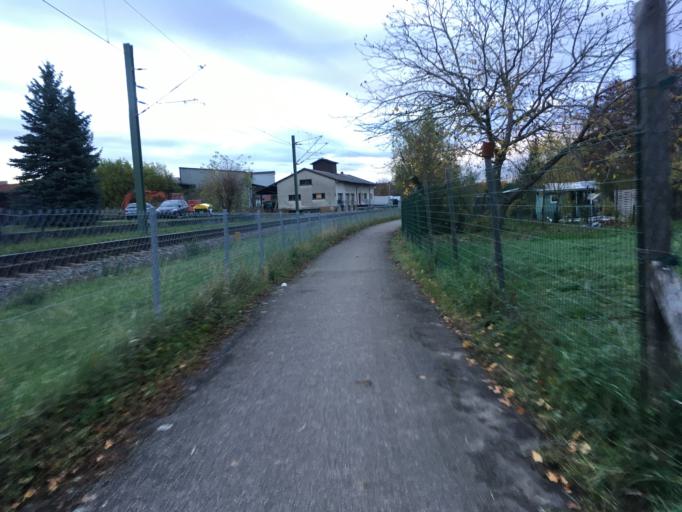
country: DE
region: Baden-Wuerttemberg
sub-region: Freiburg Region
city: Eichstetten
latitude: 48.0914
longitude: 7.7461
